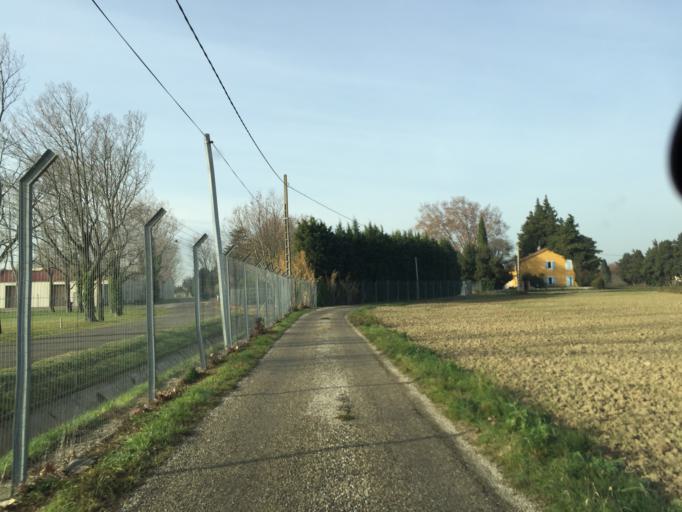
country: FR
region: Provence-Alpes-Cote d'Azur
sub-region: Departement du Vaucluse
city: Camaret-sur-Aigues
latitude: 44.1459
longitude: 4.8528
